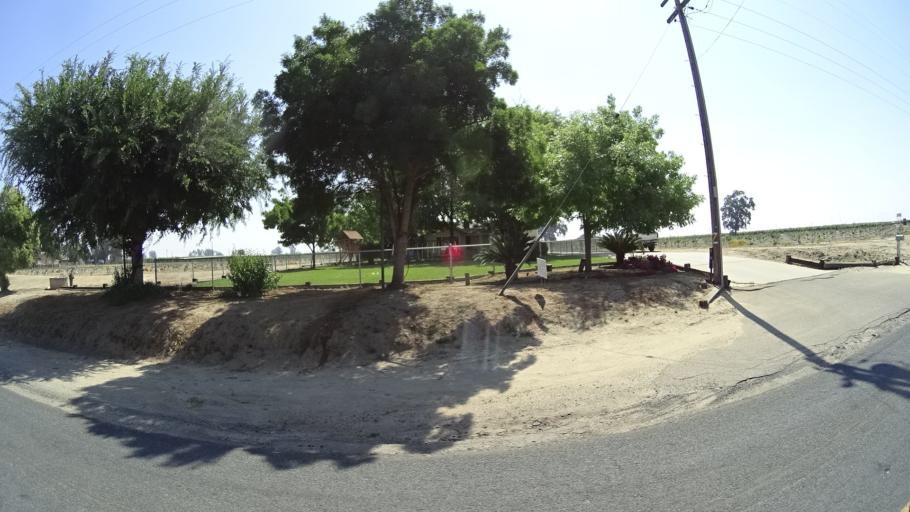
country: US
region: California
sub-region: Fresno County
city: Kingsburg
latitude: 36.4868
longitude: -119.5283
